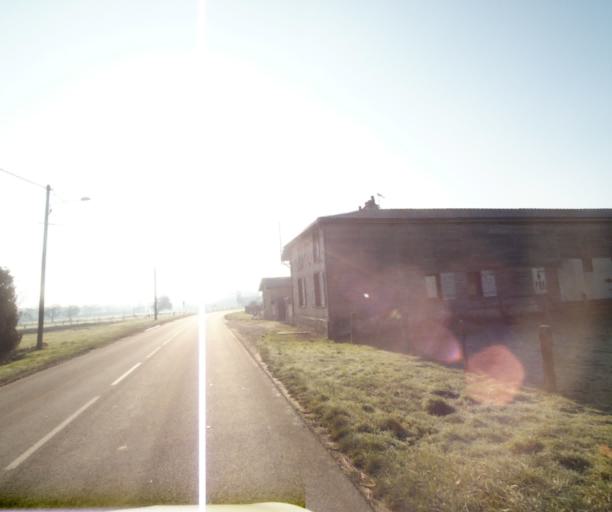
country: FR
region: Champagne-Ardenne
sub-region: Departement de la Haute-Marne
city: Montier-en-Der
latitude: 48.4585
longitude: 4.7690
